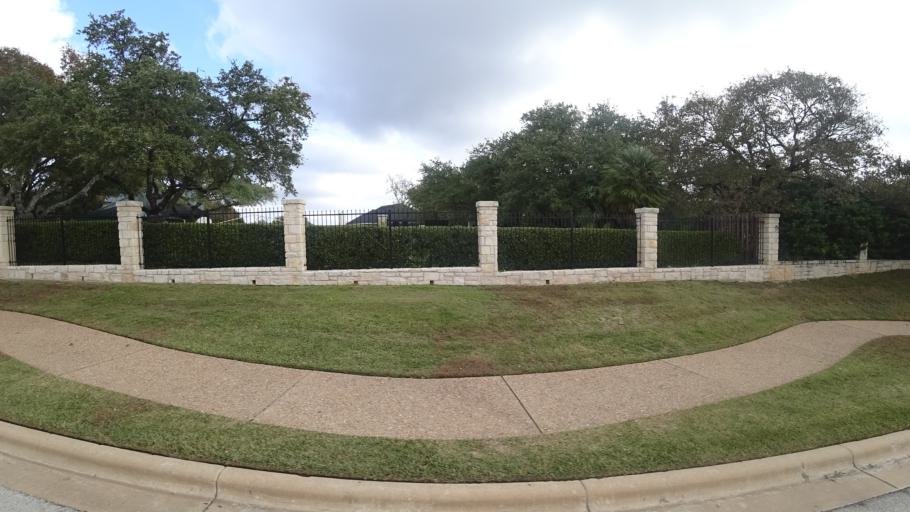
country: US
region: Texas
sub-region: Travis County
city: Barton Creek
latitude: 30.3116
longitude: -97.8980
